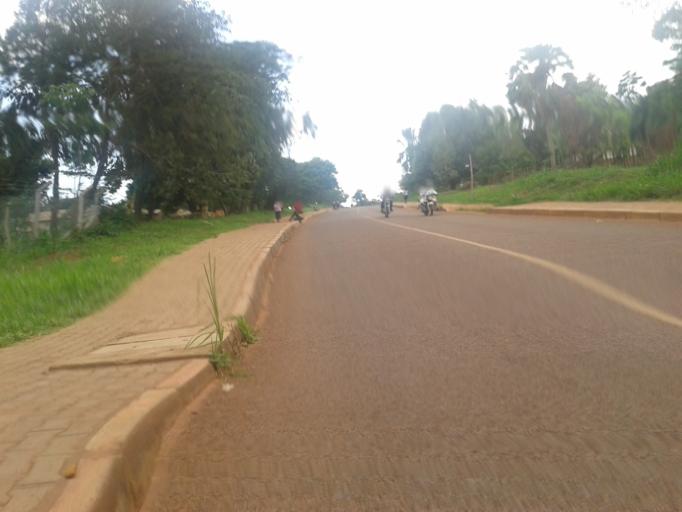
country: UG
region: Northern Region
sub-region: Gulu District
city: Gulu
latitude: 2.7643
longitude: 32.2856
